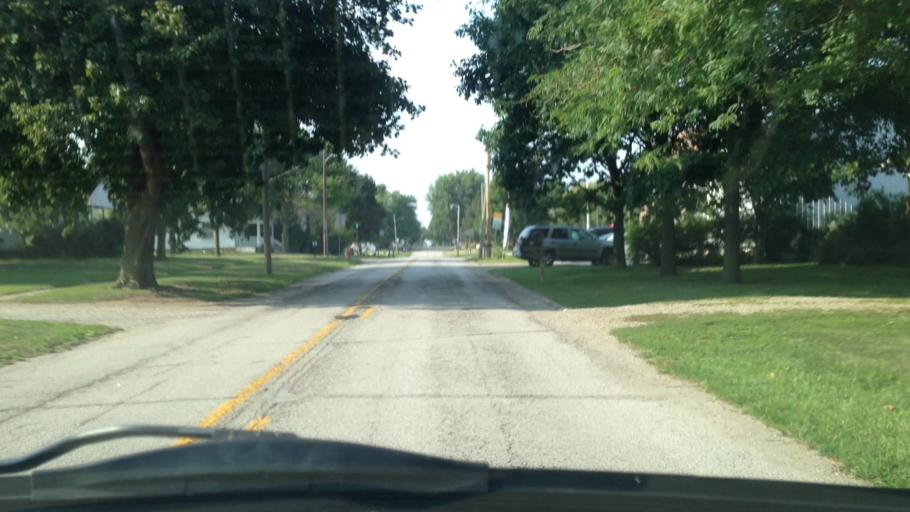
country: US
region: Iowa
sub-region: Henry County
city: Winfield
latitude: 41.2114
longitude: -91.5388
